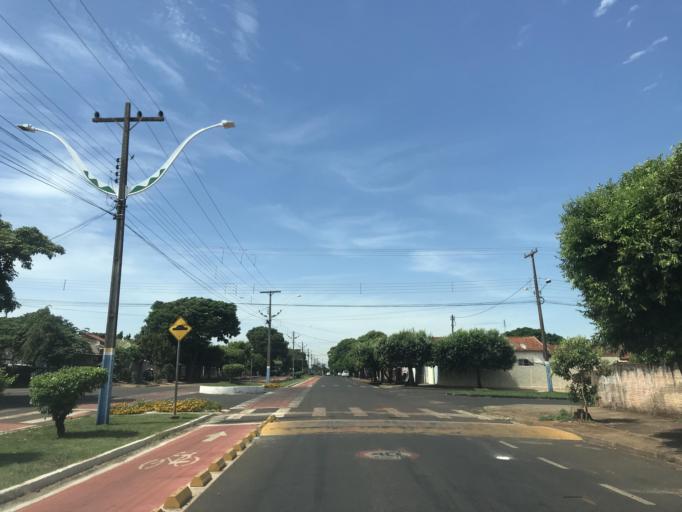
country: BR
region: Parana
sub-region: Terra Rica
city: Terra Rica
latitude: -22.7301
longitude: -52.6246
